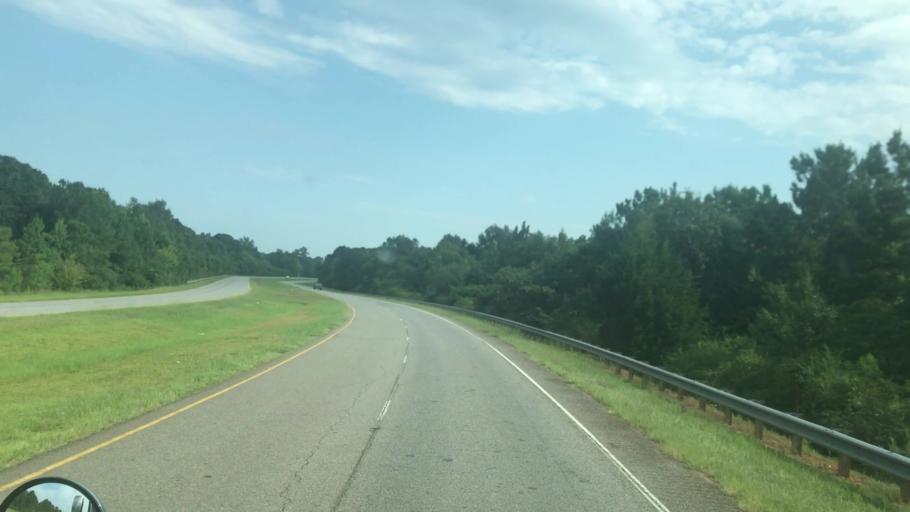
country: US
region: Georgia
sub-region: Early County
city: Blakely
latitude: 31.3671
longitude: -84.9201
